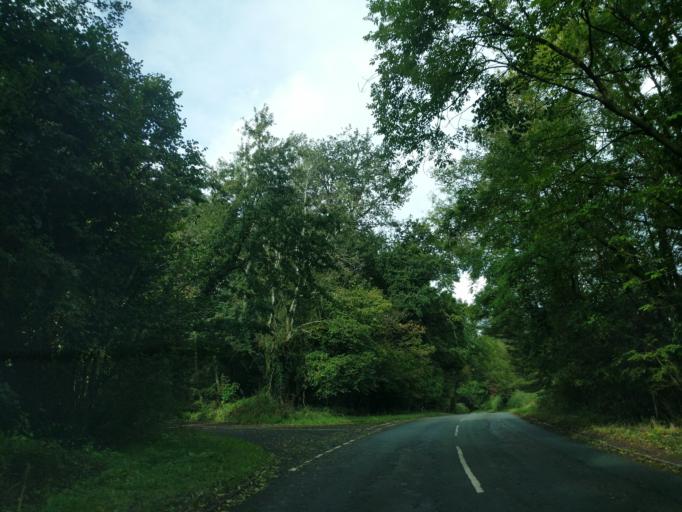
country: GB
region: England
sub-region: Staffordshire
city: Standon
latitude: 52.9733
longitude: -2.2864
